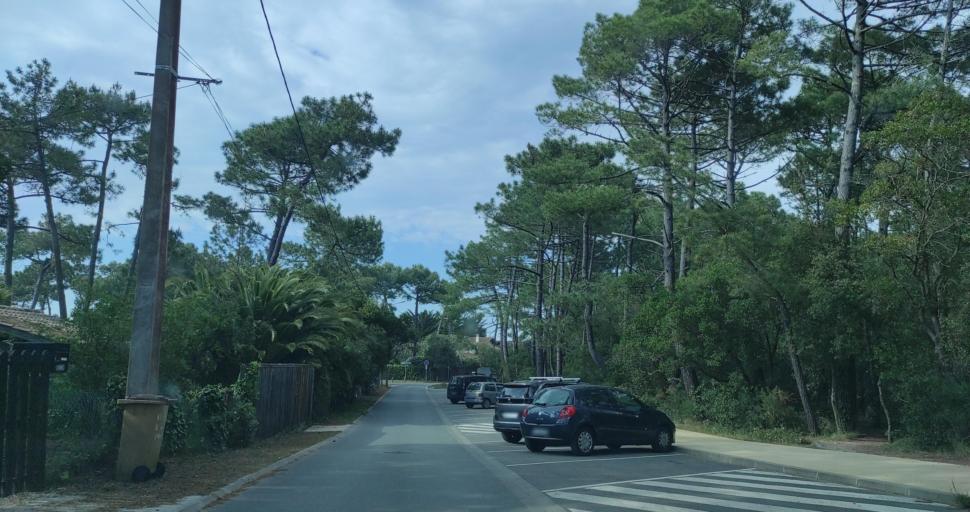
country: FR
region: Aquitaine
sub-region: Departement de la Gironde
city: Arcachon
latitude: 44.6451
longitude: -1.2499
